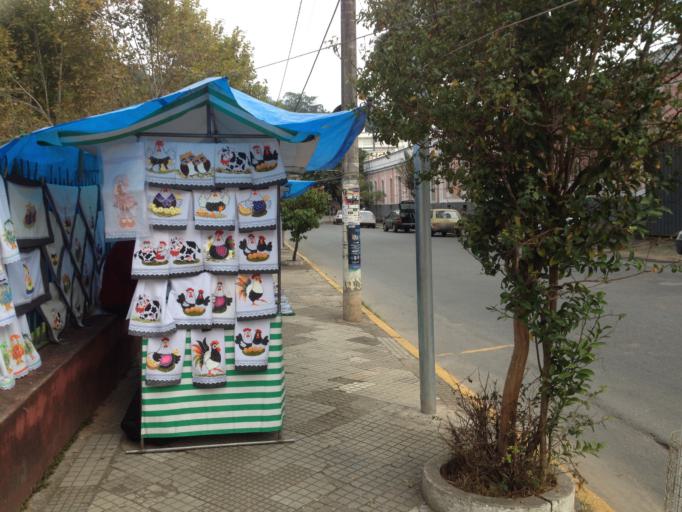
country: BR
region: Minas Gerais
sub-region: Caxambu
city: Caxambu
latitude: -21.9803
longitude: -44.9346
